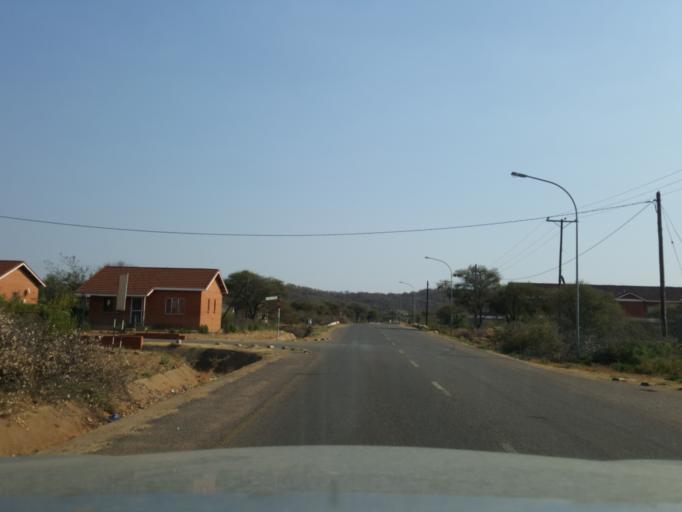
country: BW
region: South East
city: Lobatse
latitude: -25.1889
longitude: 25.6945
